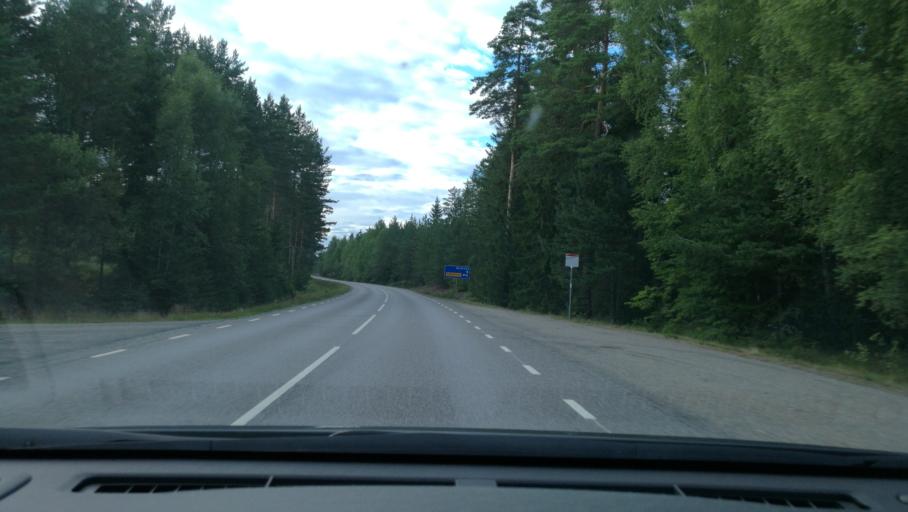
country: SE
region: OEstergoetland
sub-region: Norrkopings Kommun
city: Svartinge
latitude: 58.7540
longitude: 15.9794
